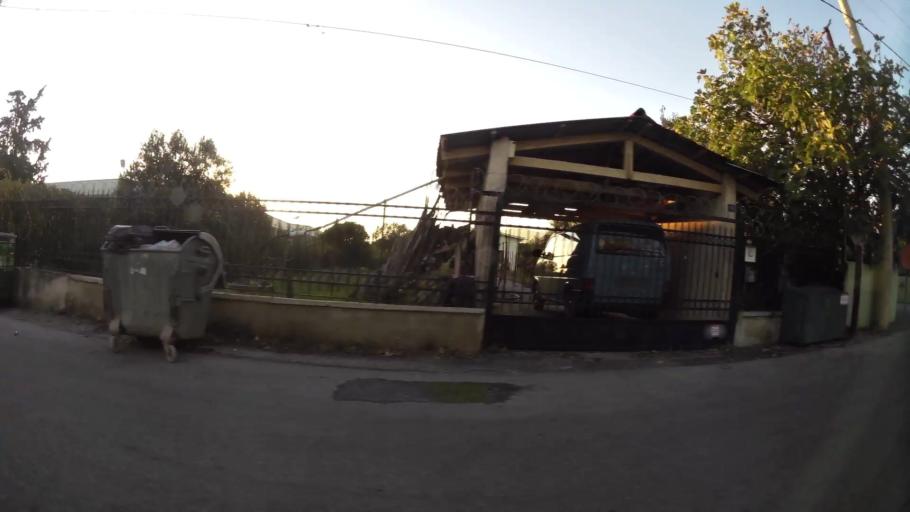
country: GR
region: Attica
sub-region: Nomarchia Anatolikis Attikis
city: Kryoneri
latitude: 38.1368
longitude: 23.8366
